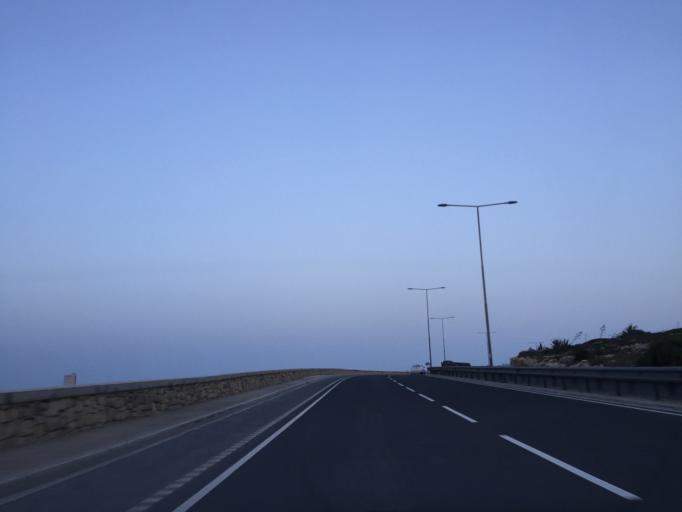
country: MT
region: Hal Gharghur
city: Hal Gharghur
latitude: 35.9469
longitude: 14.4470
